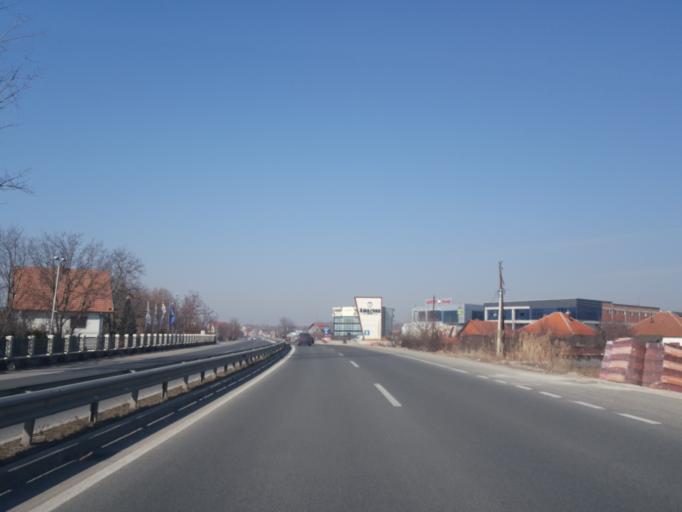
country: XK
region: Pristina
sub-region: Komuna e Obiliqit
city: Obiliq
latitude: 42.7333
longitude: 21.0706
